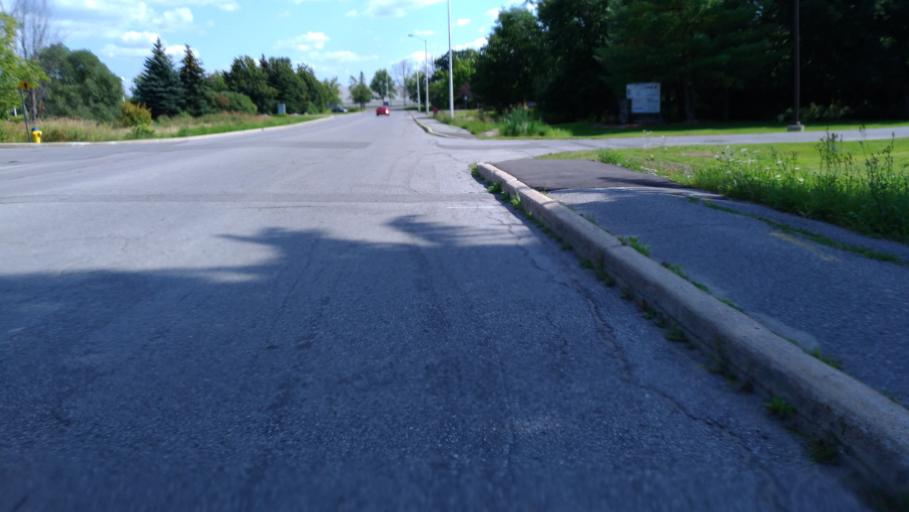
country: CA
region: Ontario
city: Bells Corners
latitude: 45.3429
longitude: -75.9207
